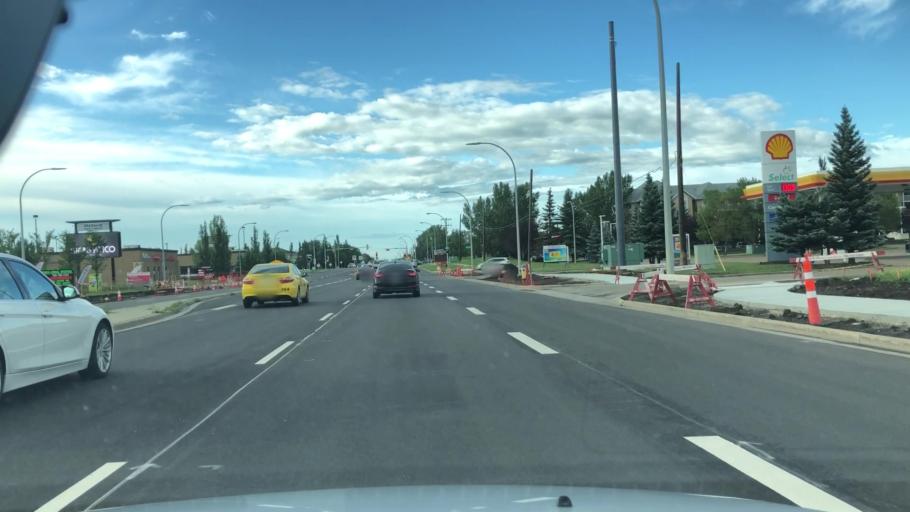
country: CA
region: Alberta
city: St. Albert
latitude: 53.6144
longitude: -113.5412
